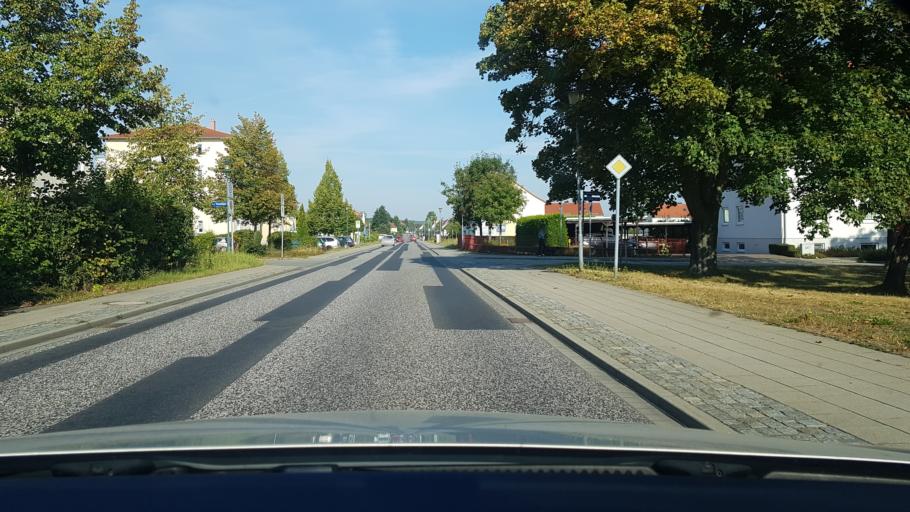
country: DE
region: Brandenburg
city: Eisenhuettenstadt
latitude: 52.1474
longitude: 14.6171
